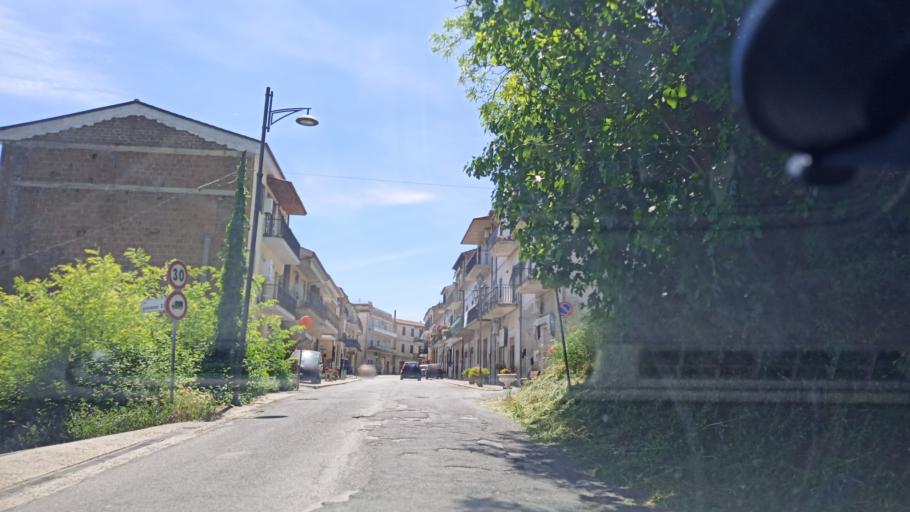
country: IT
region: Latium
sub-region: Provincia di Rieti
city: Stimigliano
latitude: 42.3019
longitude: 12.5654
